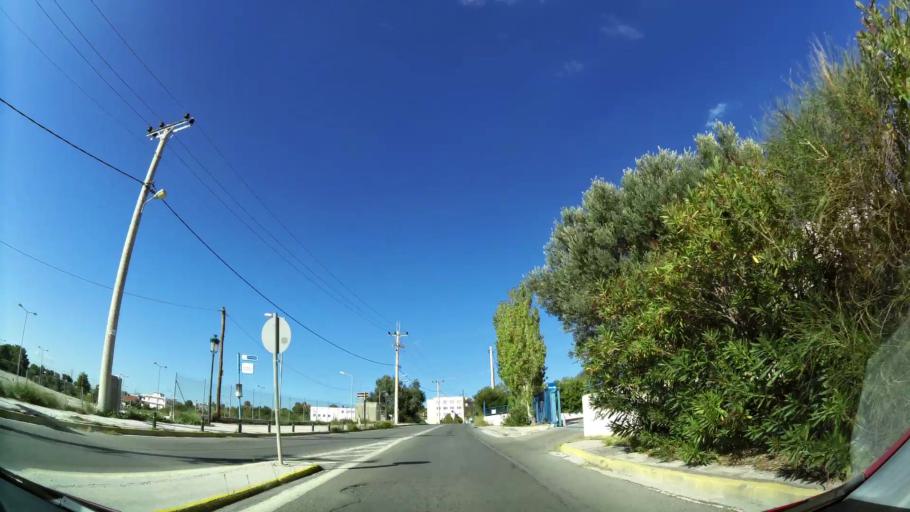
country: GR
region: Attica
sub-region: Nomarchia Anatolikis Attikis
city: Anthousa
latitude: 38.0162
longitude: 23.8719
